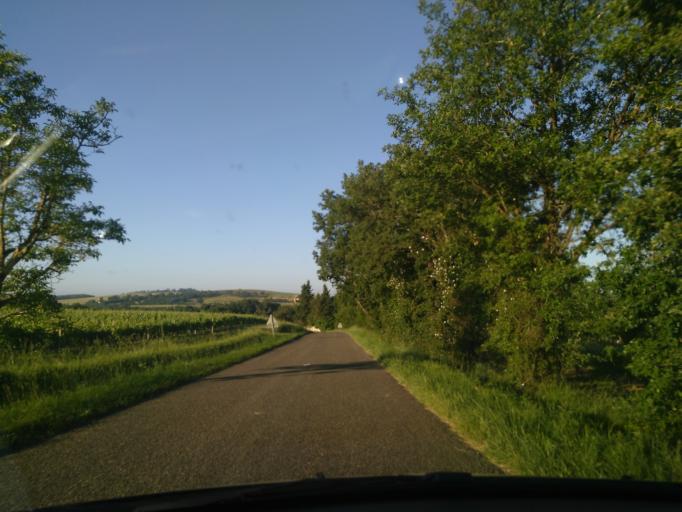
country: FR
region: Midi-Pyrenees
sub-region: Departement du Gers
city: Valence-sur-Baise
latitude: 43.8793
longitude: 0.3977
